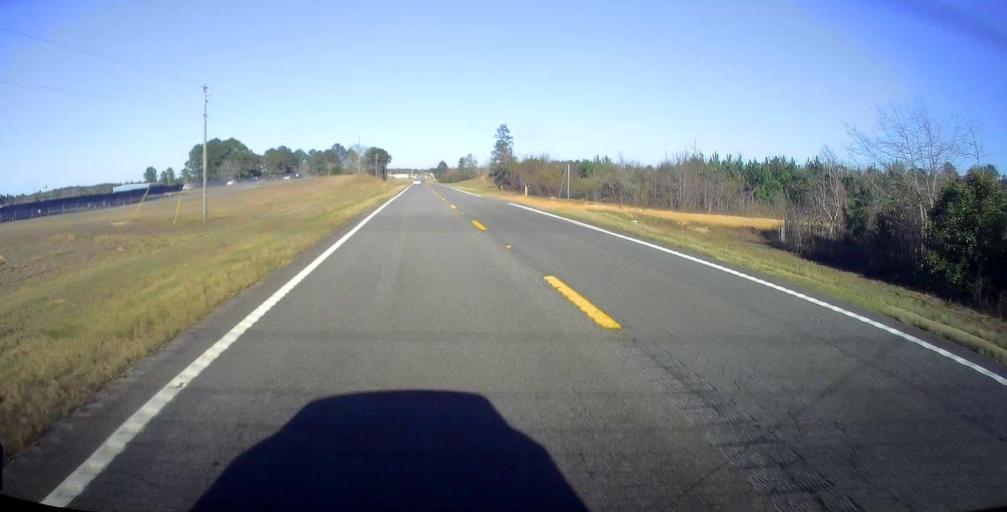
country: US
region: Georgia
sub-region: Taylor County
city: Butler
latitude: 32.5512
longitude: -84.2724
